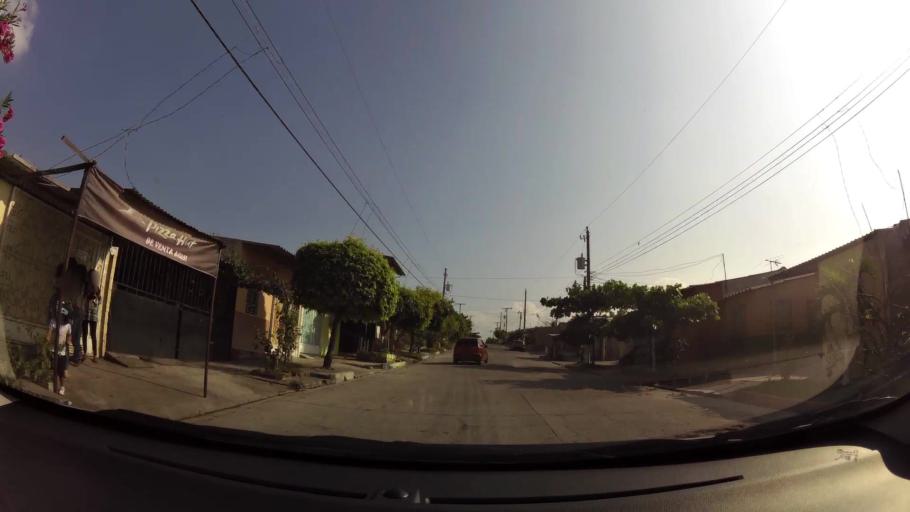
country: SV
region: San Salvador
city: Ilopango
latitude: 13.7285
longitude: -89.1118
